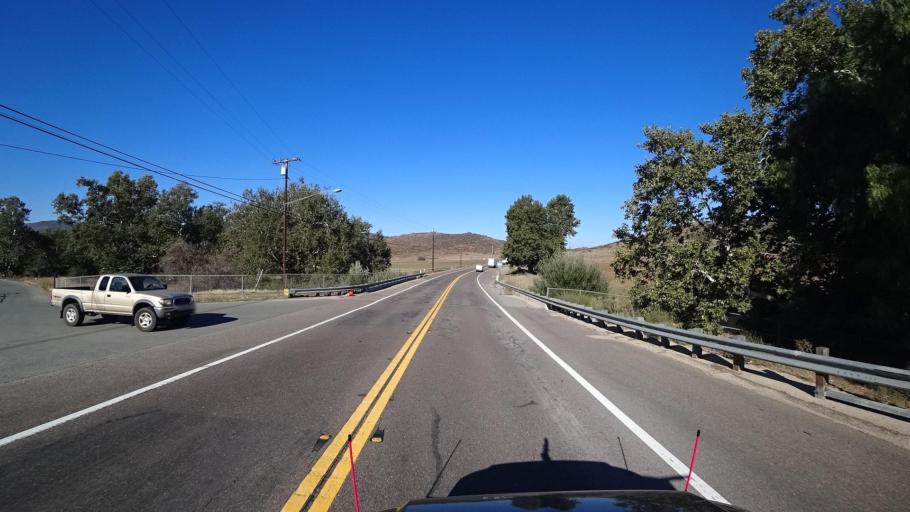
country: US
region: California
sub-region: San Diego County
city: Jamul
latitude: 32.6845
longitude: -116.8466
